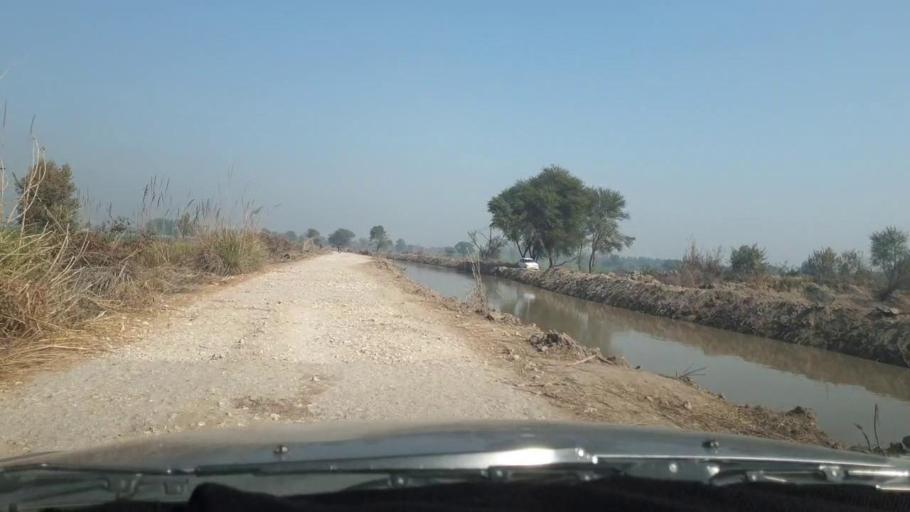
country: PK
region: Sindh
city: Khanpur
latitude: 27.7928
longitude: 69.5622
